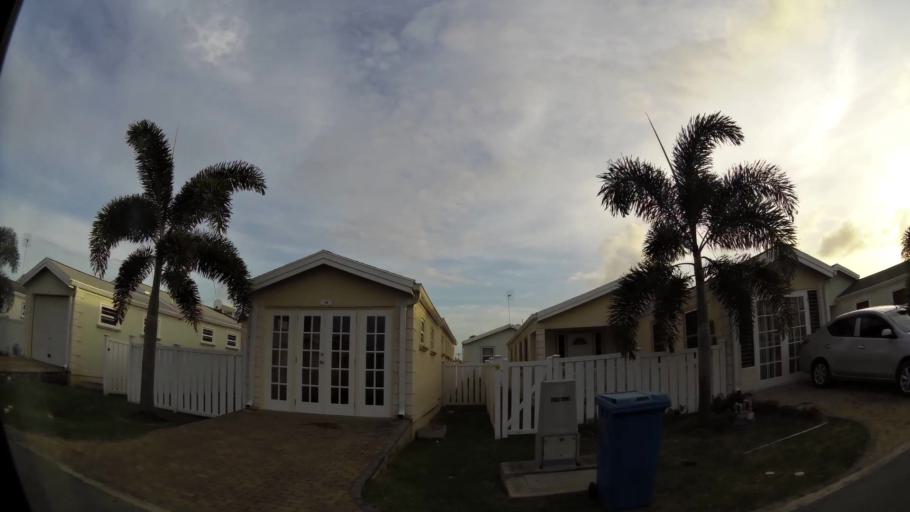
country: BB
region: Christ Church
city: Oistins
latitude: 13.0869
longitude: -59.5012
